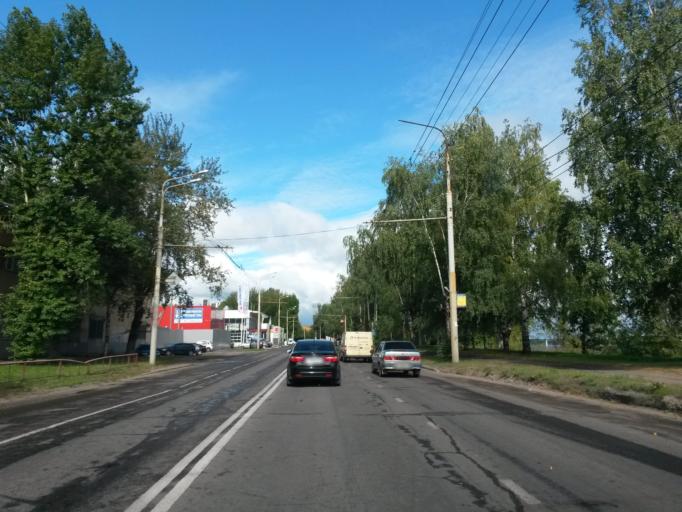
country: RU
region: Jaroslavl
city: Yaroslavl
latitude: 57.6589
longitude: 39.8630
